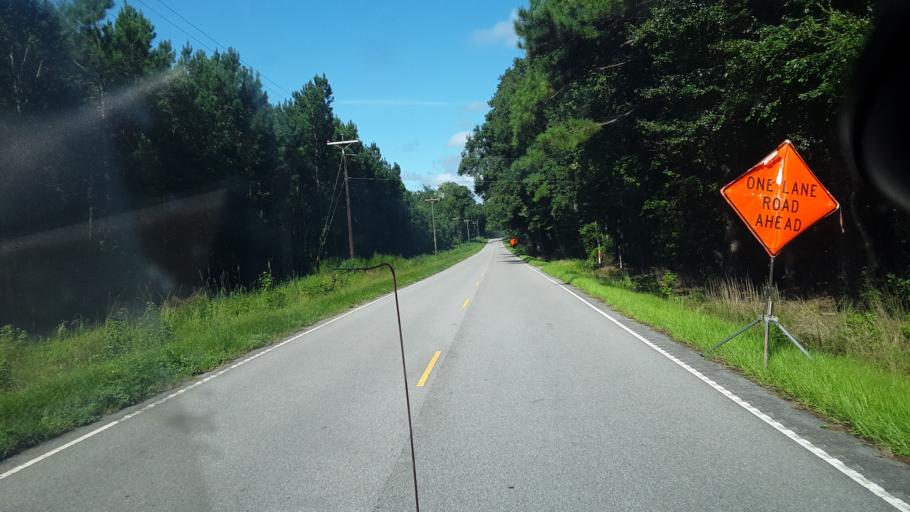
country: US
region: South Carolina
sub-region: Jasper County
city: Ridgeland
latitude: 32.5892
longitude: -80.9409
